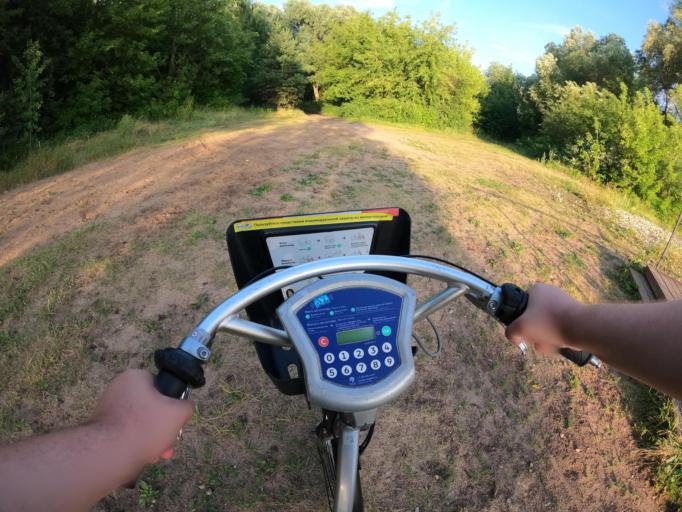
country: RU
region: Moscow
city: Strogino
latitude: 55.8244
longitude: 37.4026
